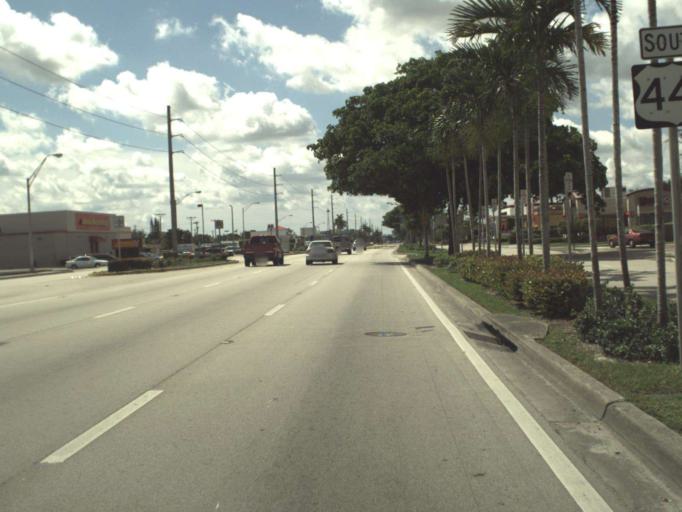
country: US
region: Florida
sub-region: Miami-Dade County
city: Norland
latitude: 25.9560
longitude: -80.2058
